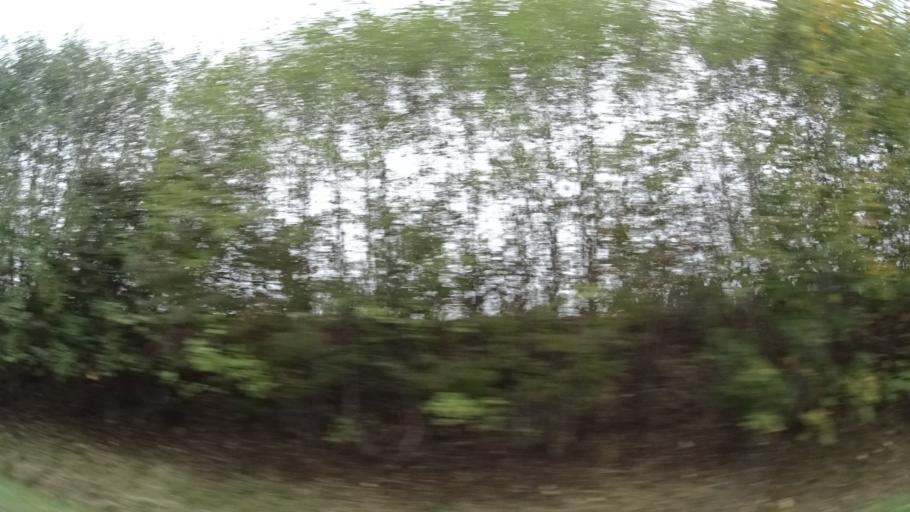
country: DE
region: Hesse
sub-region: Regierungsbezirk Kassel
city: Poppenhausen
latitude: 50.5127
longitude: 9.8797
